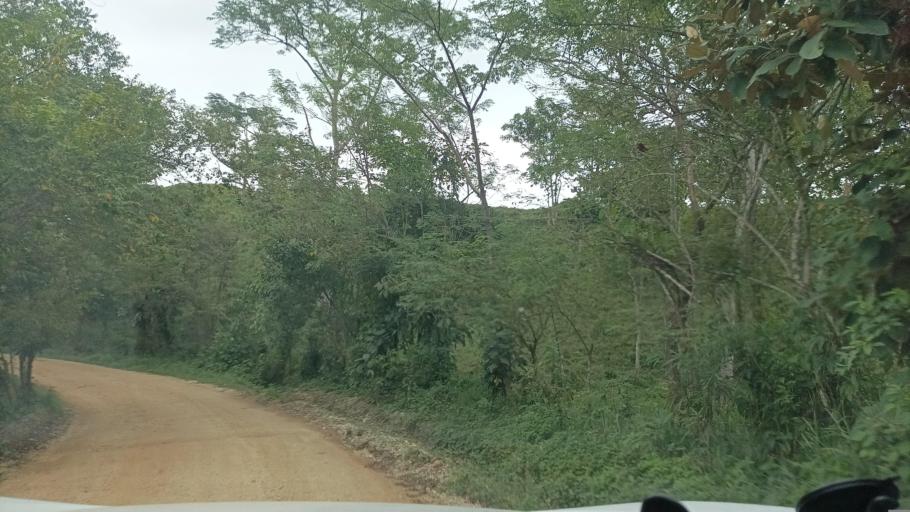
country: MX
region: Veracruz
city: Hidalgotitlan
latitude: 17.6048
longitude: -94.5280
